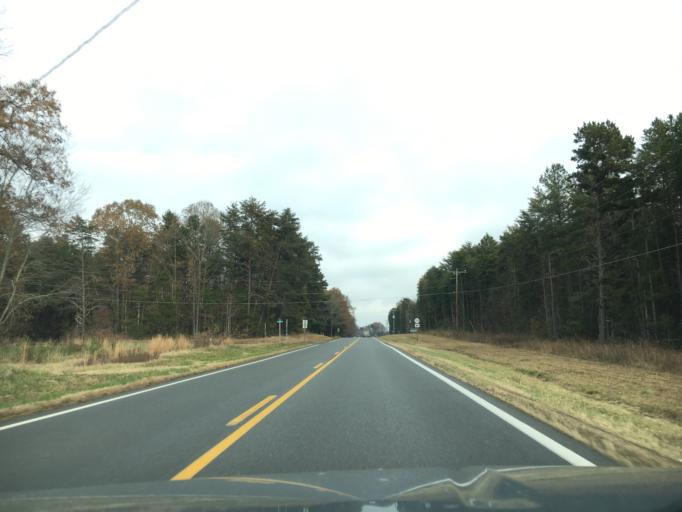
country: US
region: Virginia
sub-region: Prince Edward County
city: Farmville
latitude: 37.3634
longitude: -78.3756
